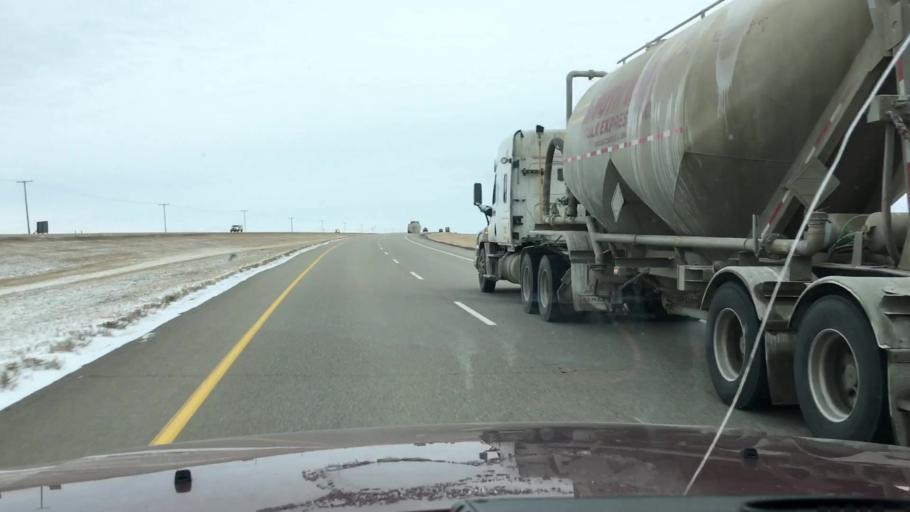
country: CA
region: Saskatchewan
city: Watrous
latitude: 51.2340
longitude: -105.9620
